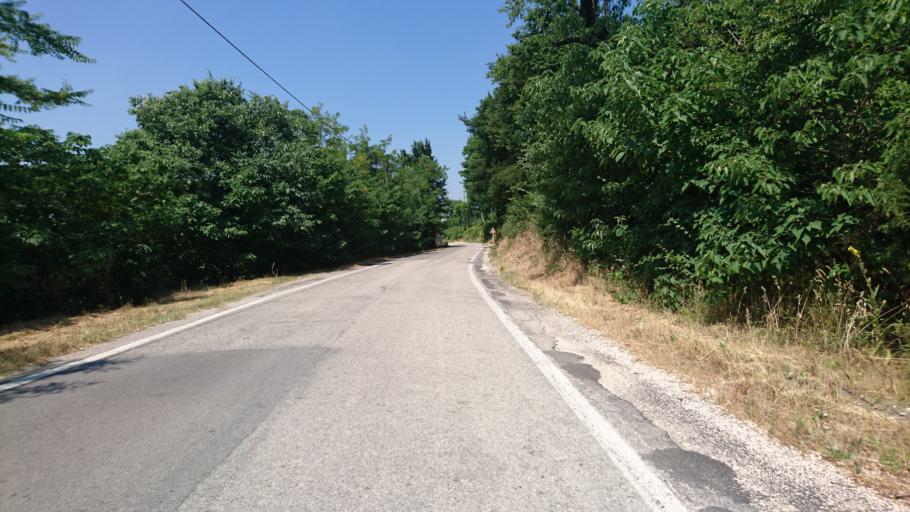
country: IT
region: Veneto
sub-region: Provincia di Vicenza
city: Albettone
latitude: 45.3669
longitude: 11.5941
